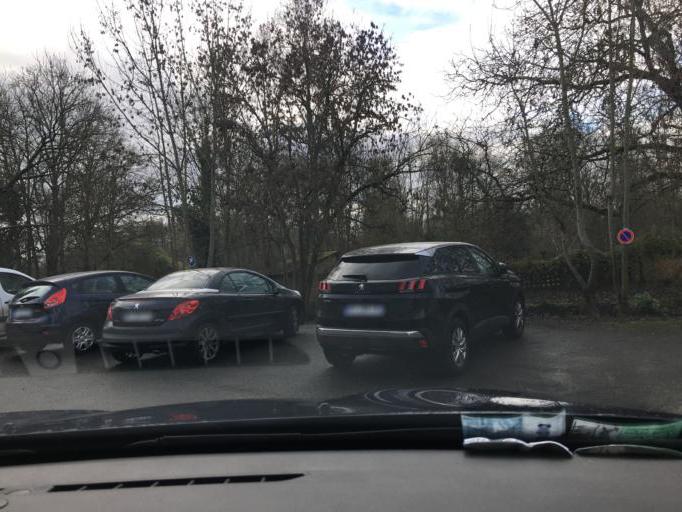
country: FR
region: Centre
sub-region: Departement du Loiret
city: Meung-sur-Loire
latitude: 47.8432
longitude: 1.7026
